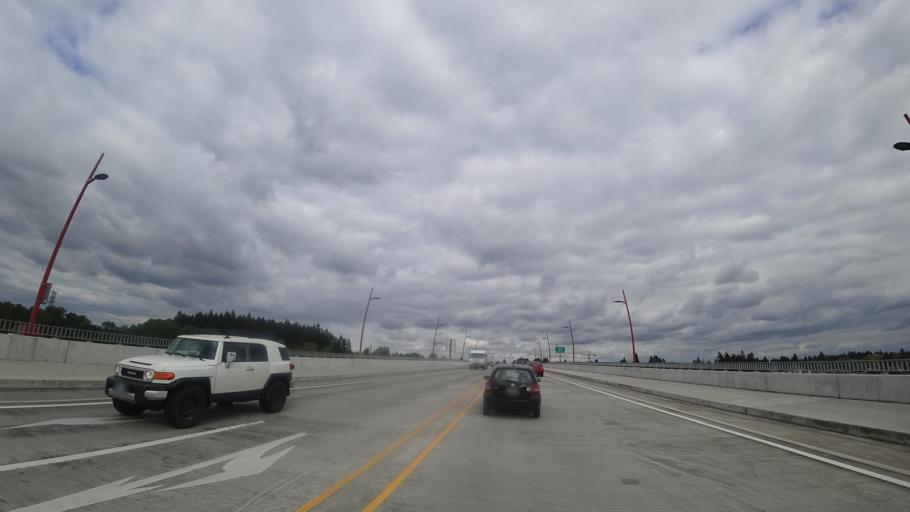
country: US
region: Oregon
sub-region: Clackamas County
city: Milwaukie
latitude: 45.4642
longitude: -122.6664
